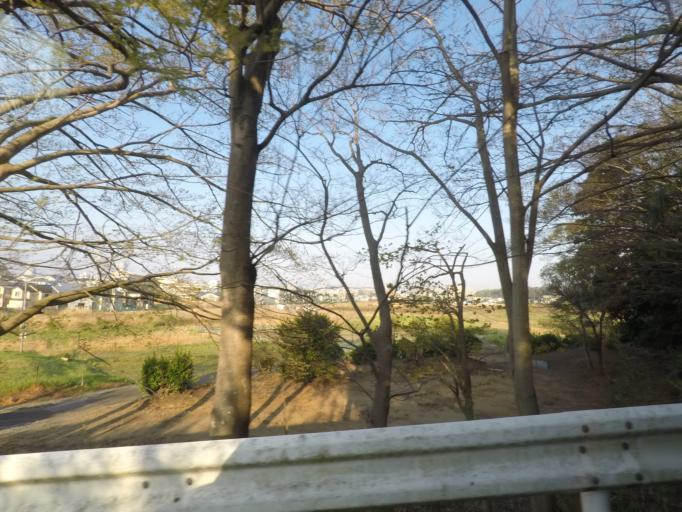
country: JP
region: Chiba
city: Chiba
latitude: 35.6193
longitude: 140.1415
